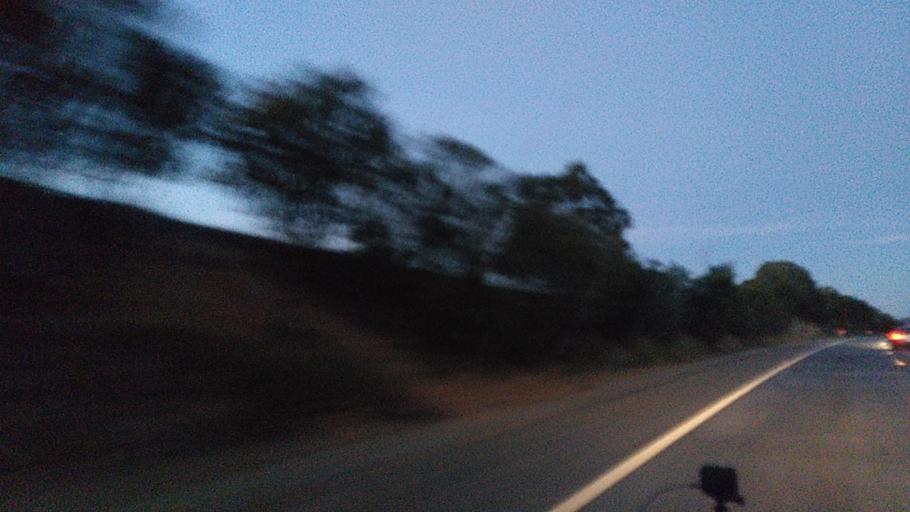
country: AU
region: New South Wales
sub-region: Wingecarribee
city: Moss Vale
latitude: -34.5132
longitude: 150.3062
